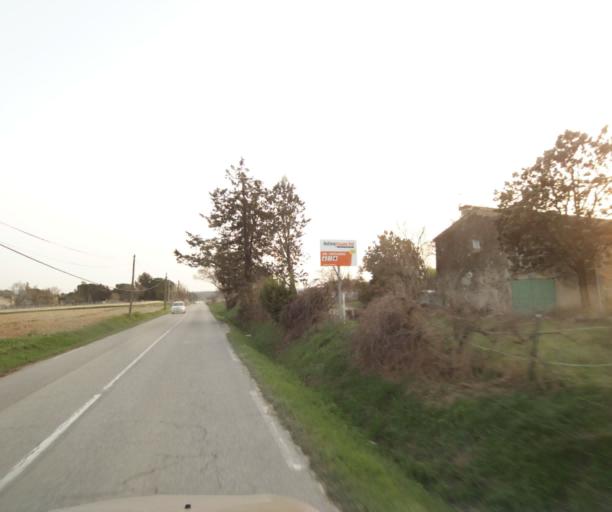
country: FR
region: Provence-Alpes-Cote d'Azur
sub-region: Departement des Bouches-du-Rhone
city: Eguilles
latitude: 43.5523
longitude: 5.3498
